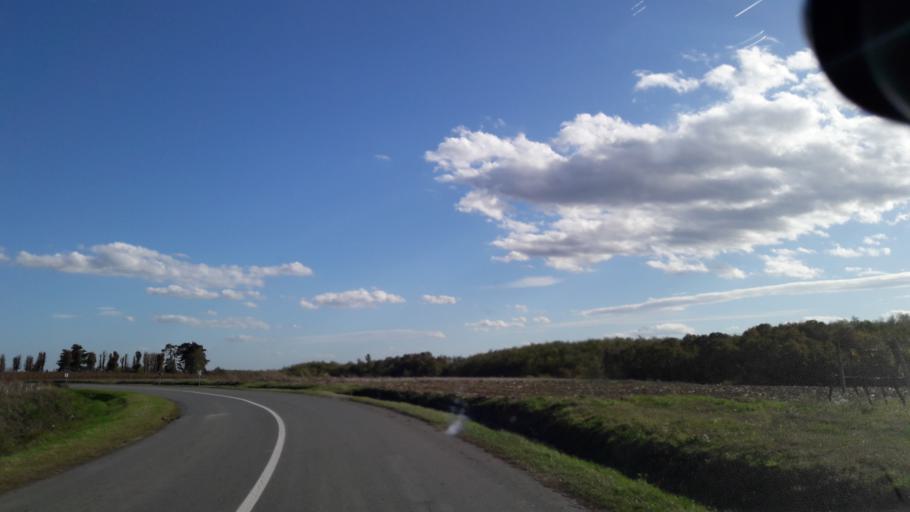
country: HR
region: Osjecko-Baranjska
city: Gorjani
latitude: 45.3808
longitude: 18.2598
